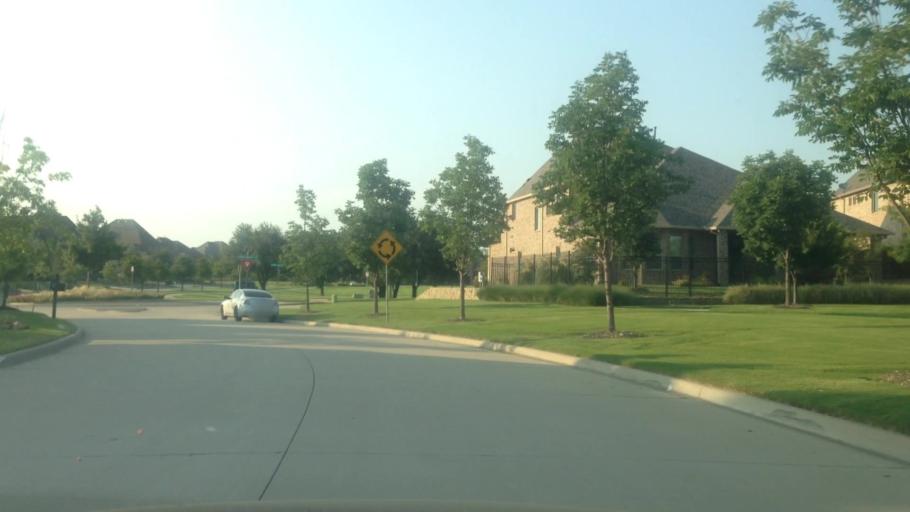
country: US
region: Texas
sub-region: Denton County
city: The Colony
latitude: 33.1307
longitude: -96.8783
